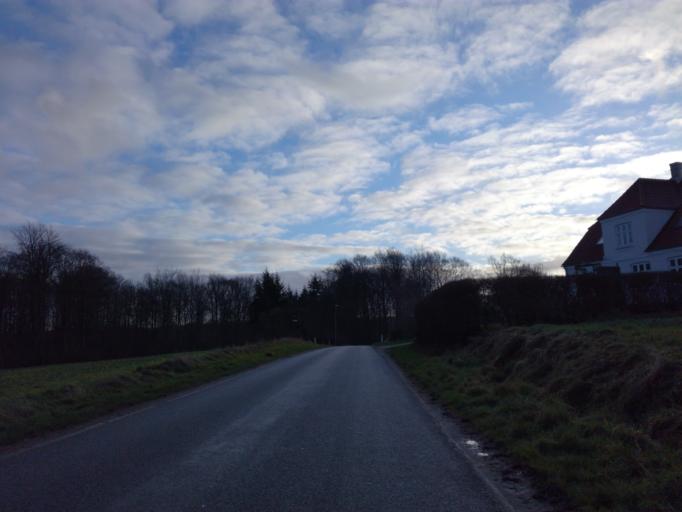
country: DK
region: South Denmark
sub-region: Fredericia Kommune
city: Taulov
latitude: 55.5533
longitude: 9.6025
